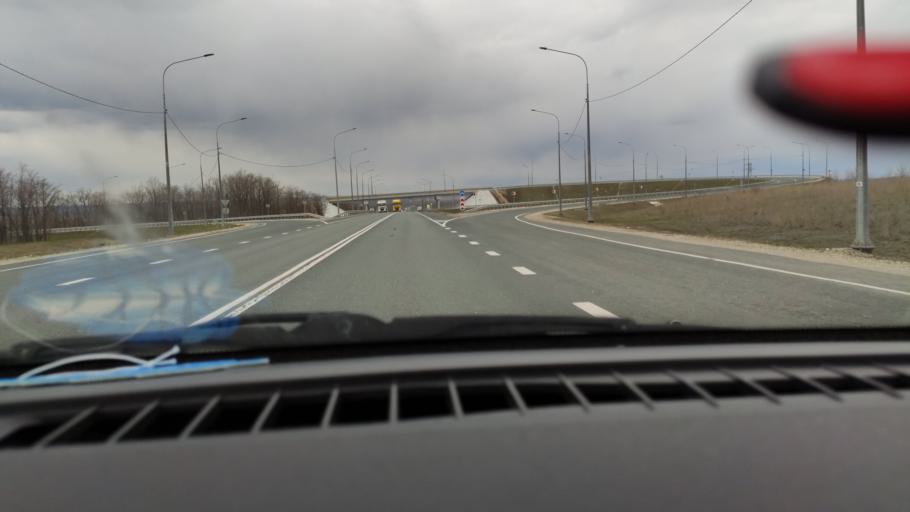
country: RU
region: Saratov
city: Yelshanka
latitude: 51.8255
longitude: 46.2913
